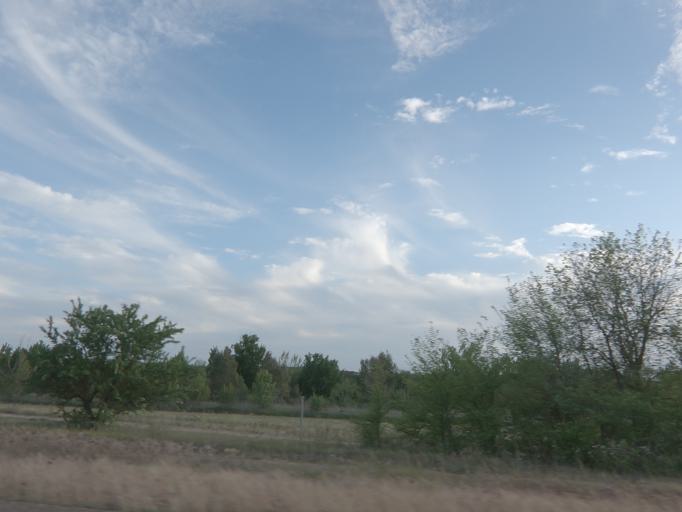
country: ES
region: Extremadura
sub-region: Provincia de Badajoz
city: Lobon
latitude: 38.8430
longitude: -6.6728
